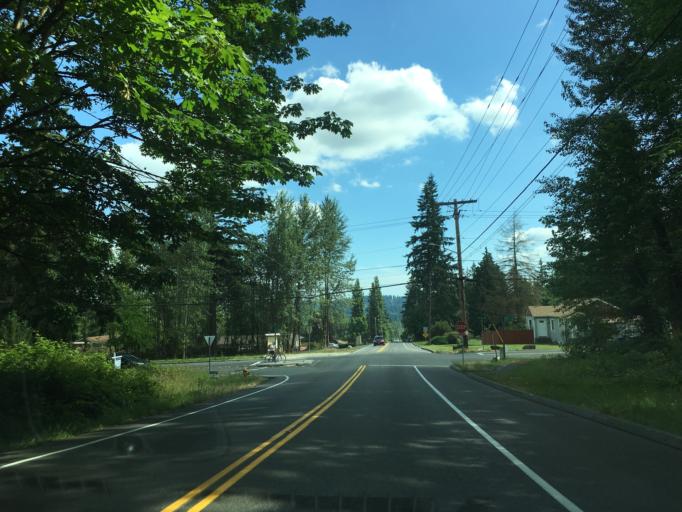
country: US
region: Washington
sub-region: King County
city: Kenmore
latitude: 47.7809
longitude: -122.2330
